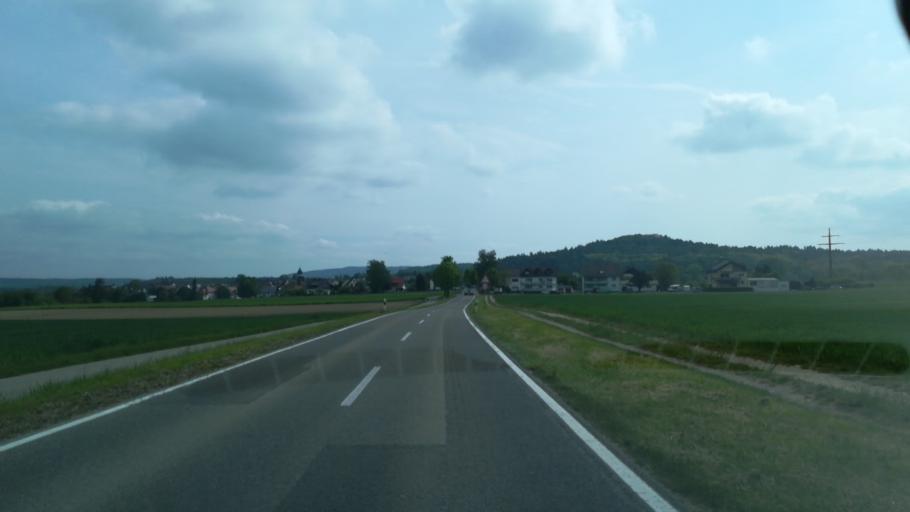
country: DE
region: Baden-Wuerttemberg
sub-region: Freiburg Region
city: Singen
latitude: 47.7812
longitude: 8.8681
